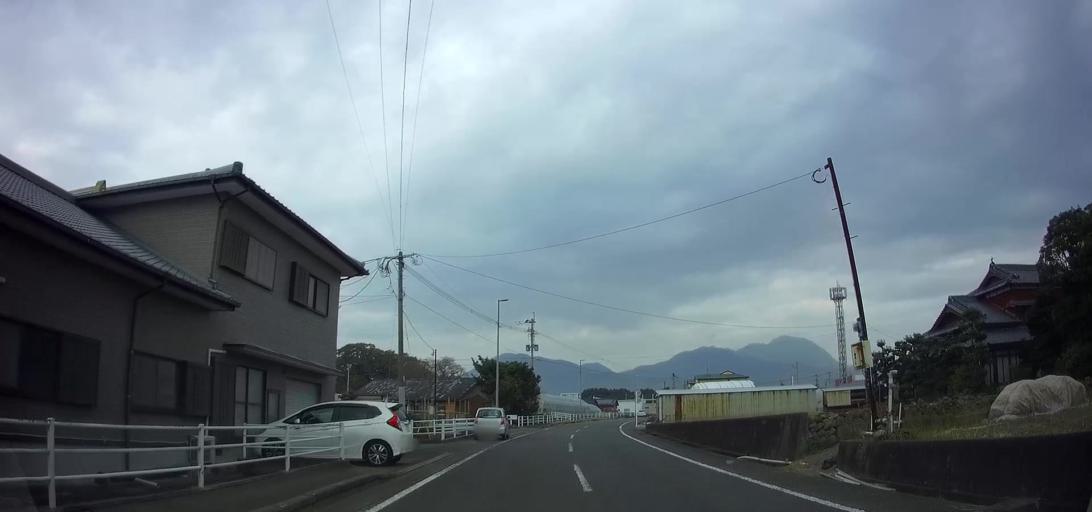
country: JP
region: Nagasaki
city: Shimabara
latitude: 32.6599
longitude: 130.3110
